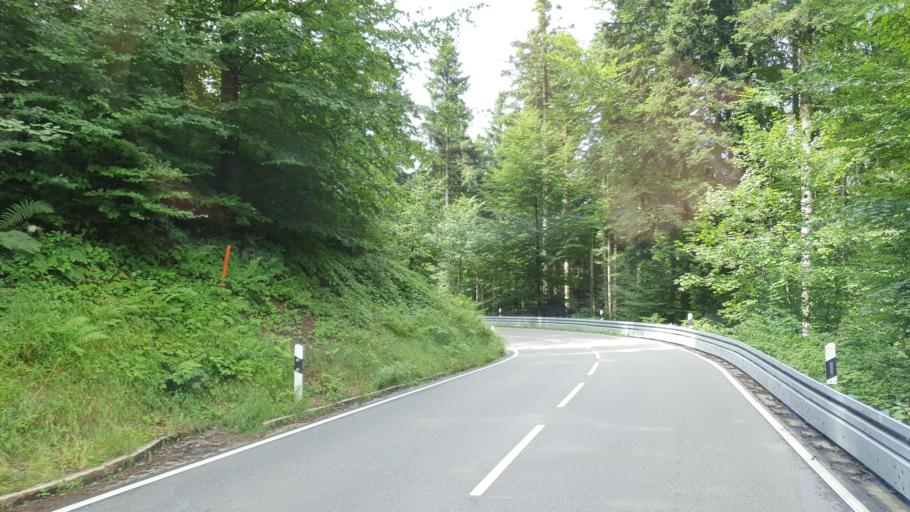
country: AT
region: Vorarlberg
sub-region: Politischer Bezirk Bregenz
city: Moggers
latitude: 47.5945
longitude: 9.8147
